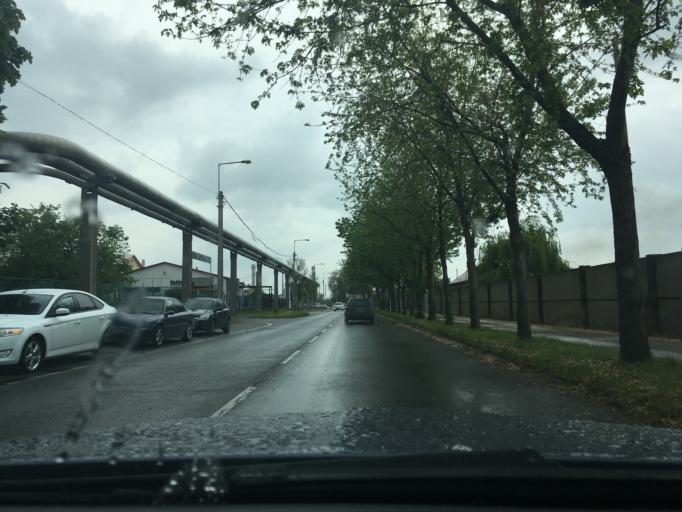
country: HU
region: Hajdu-Bihar
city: Debrecen
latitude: 47.5119
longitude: 21.6393
